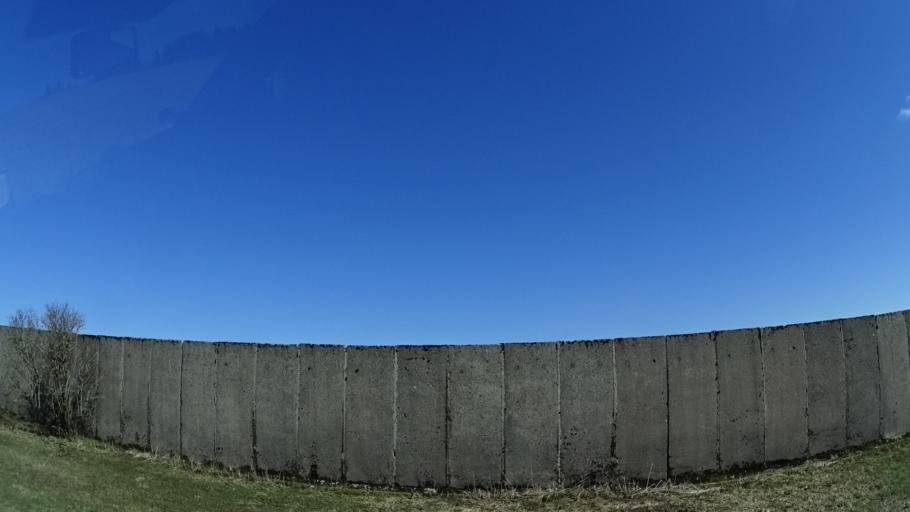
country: DE
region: Thuringia
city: Steinheid
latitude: 50.4566
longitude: 11.0995
